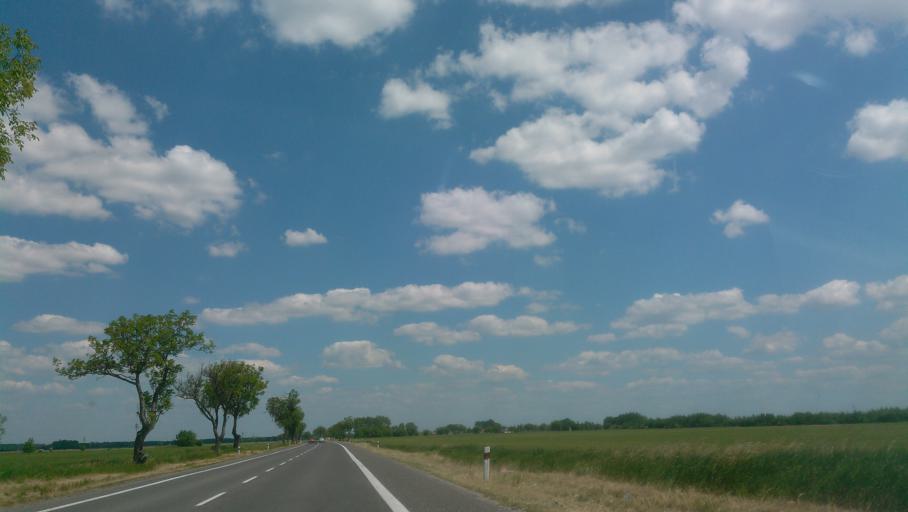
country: SK
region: Trnavsky
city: Dunajska Streda
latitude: 48.0003
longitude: 17.4631
